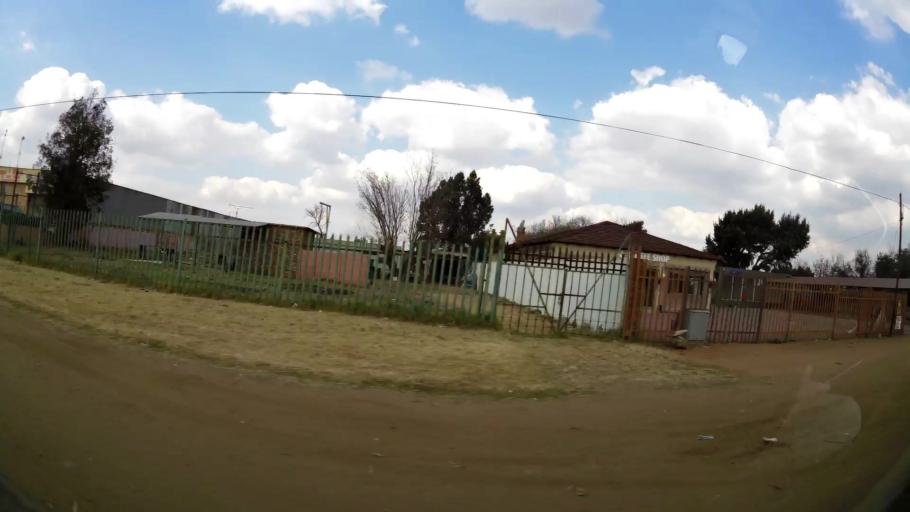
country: ZA
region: Gauteng
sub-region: Ekurhuleni Metropolitan Municipality
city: Benoni
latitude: -26.1098
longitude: 28.3666
